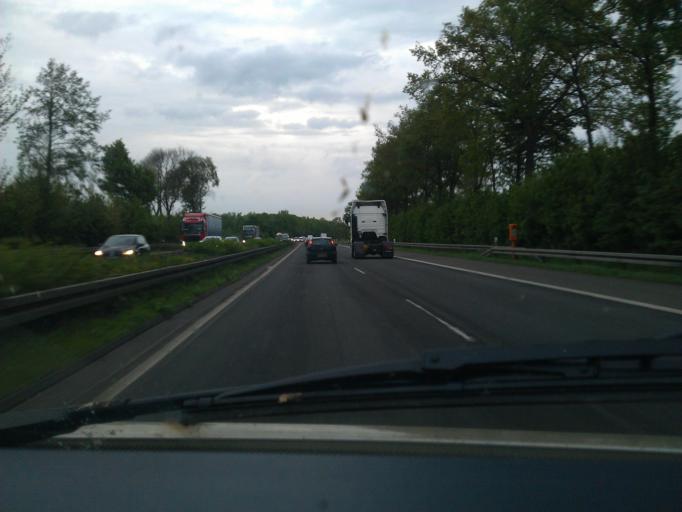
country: DE
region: North Rhine-Westphalia
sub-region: Regierungsbezirk Koln
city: Alsdorf
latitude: 50.8425
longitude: 6.1940
